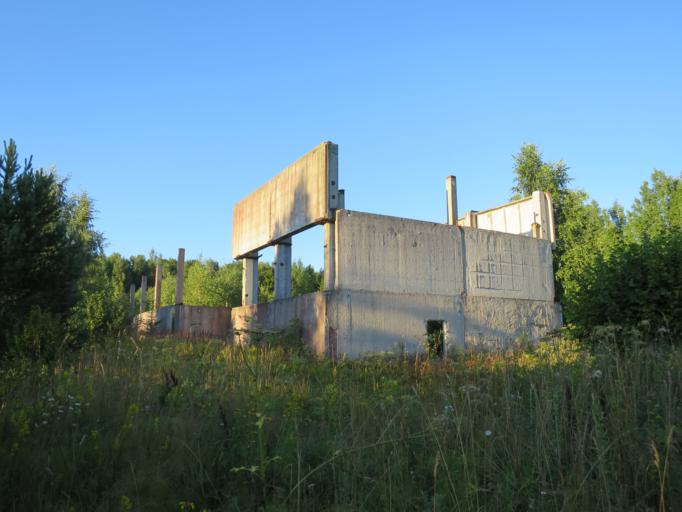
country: LV
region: Sigulda
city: Sigulda
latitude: 57.1432
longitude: 24.9481
